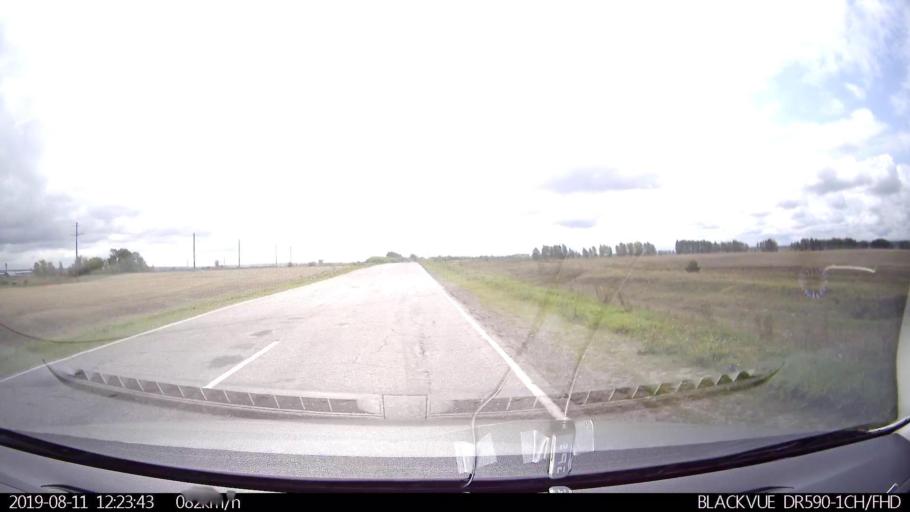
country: RU
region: Ulyanovsk
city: Ignatovka
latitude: 53.8901
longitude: 47.9511
